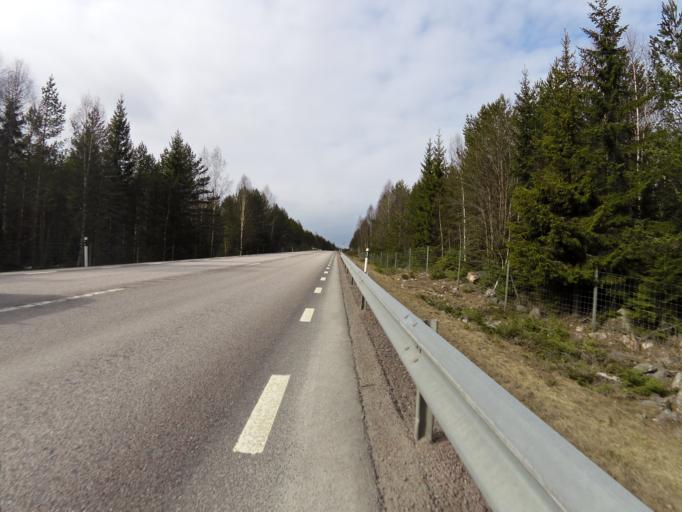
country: SE
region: Gaevleborg
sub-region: Hofors Kommun
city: Hofors
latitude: 60.5429
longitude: 16.1620
